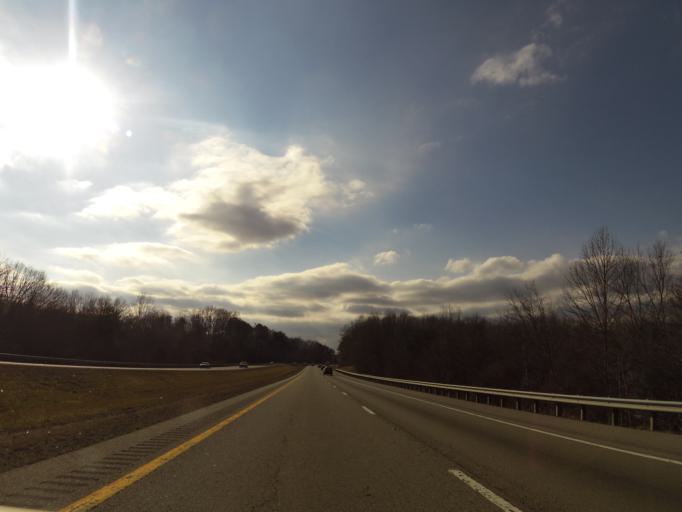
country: US
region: Tennessee
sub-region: Cumberland County
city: Crossville
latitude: 35.9588
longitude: -84.9676
